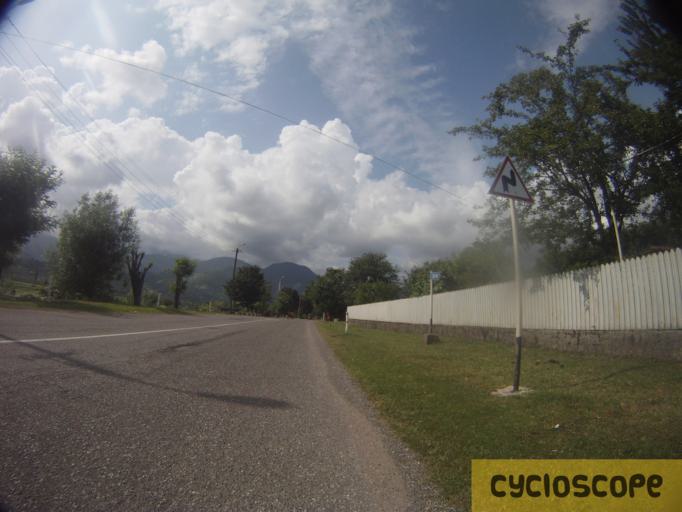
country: GE
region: Samegrelo and Zemo Svaneti
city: Tsalenjikha
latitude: 42.6271
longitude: 41.9766
